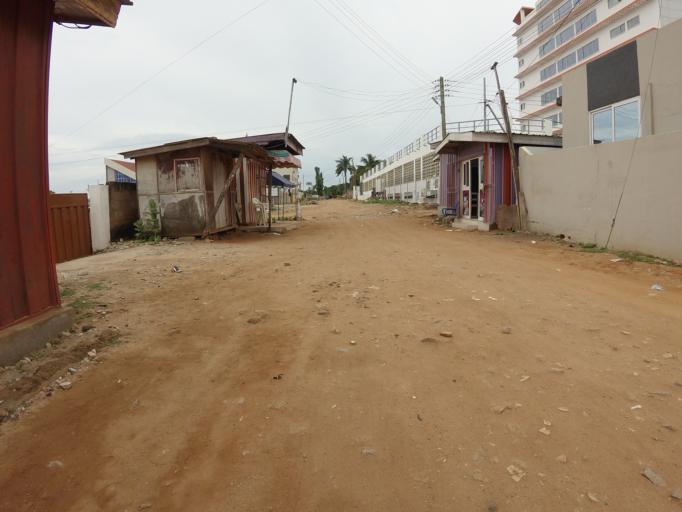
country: GH
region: Greater Accra
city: Accra
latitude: 5.5993
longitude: -0.2233
